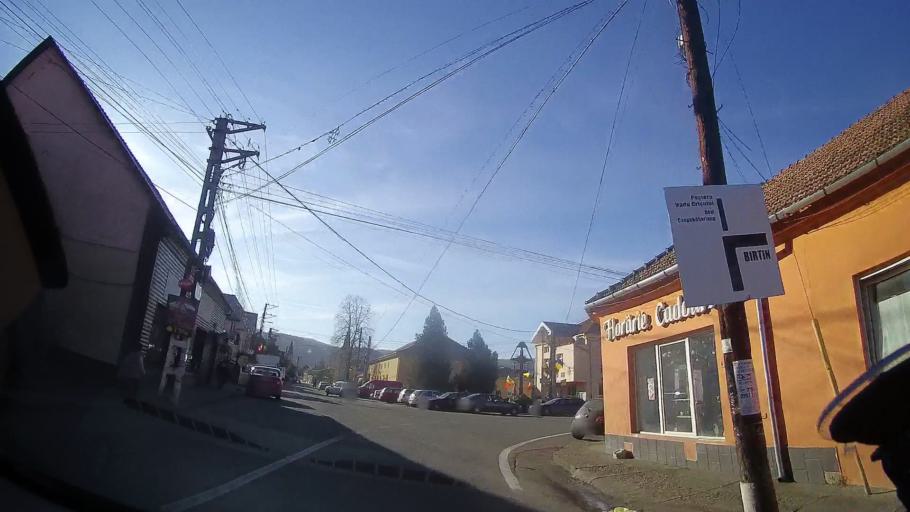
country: RO
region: Bihor
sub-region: Comuna Vadu Crisului
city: Vadu Crisului
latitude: 46.9859
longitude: 22.5155
